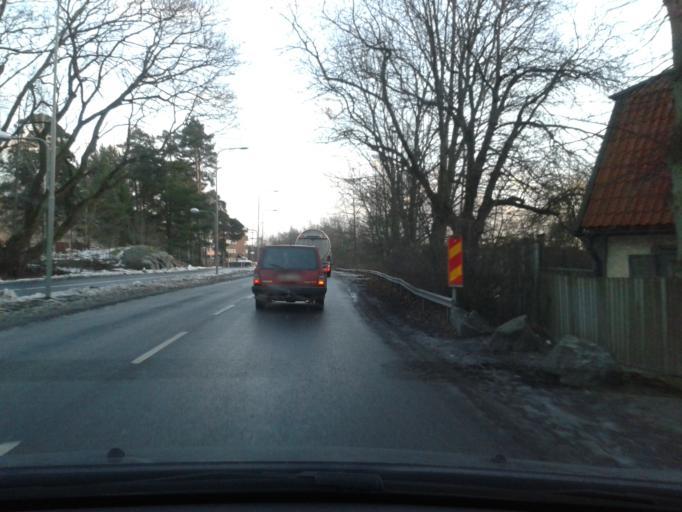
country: SE
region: Stockholm
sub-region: Stockholms Kommun
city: Arsta
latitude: 59.2626
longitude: 18.1017
